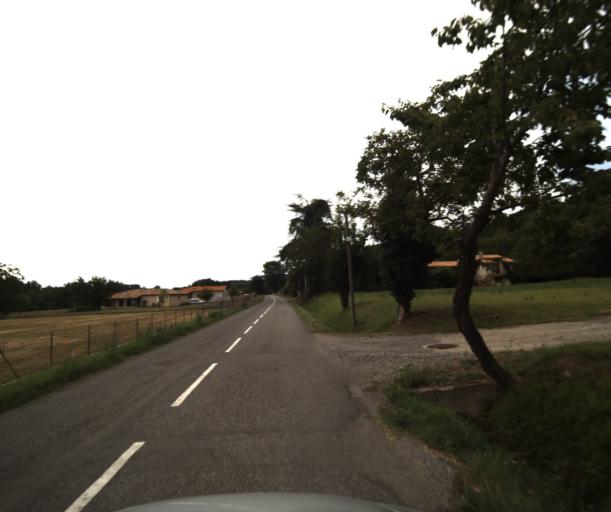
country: FR
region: Midi-Pyrenees
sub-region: Departement de la Haute-Garonne
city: Eaunes
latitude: 43.4239
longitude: 1.3188
